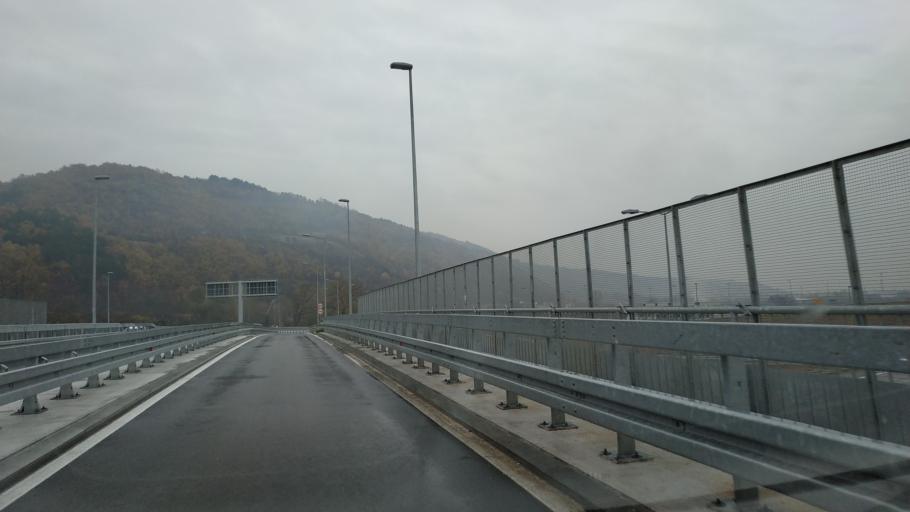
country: RS
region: Central Serbia
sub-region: Pirotski Okrug
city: Pirot
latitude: 43.1878
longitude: 22.5631
